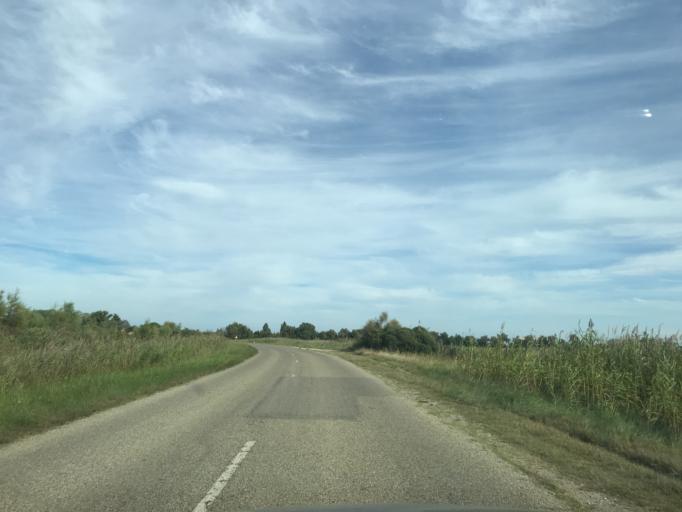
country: FR
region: Provence-Alpes-Cote d'Azur
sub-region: Departement des Bouches-du-Rhone
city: Saintes-Maries-de-la-Mer
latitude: 43.5200
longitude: 4.3922
